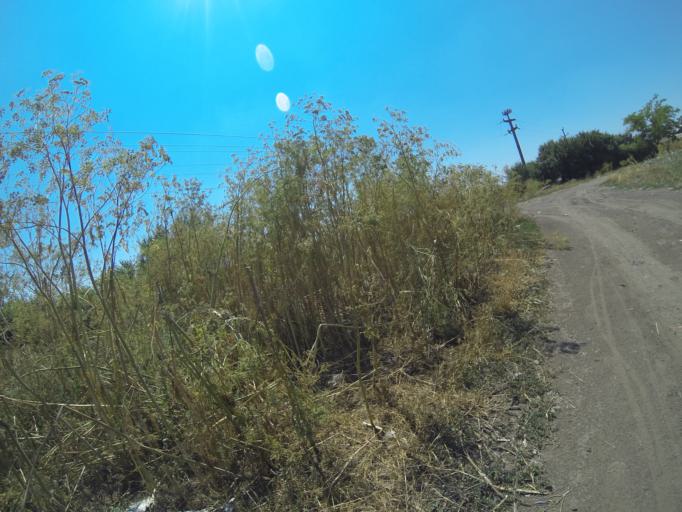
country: RO
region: Dolj
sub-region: Comuna Segarcea
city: Segarcea
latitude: 44.0865
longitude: 23.7543
